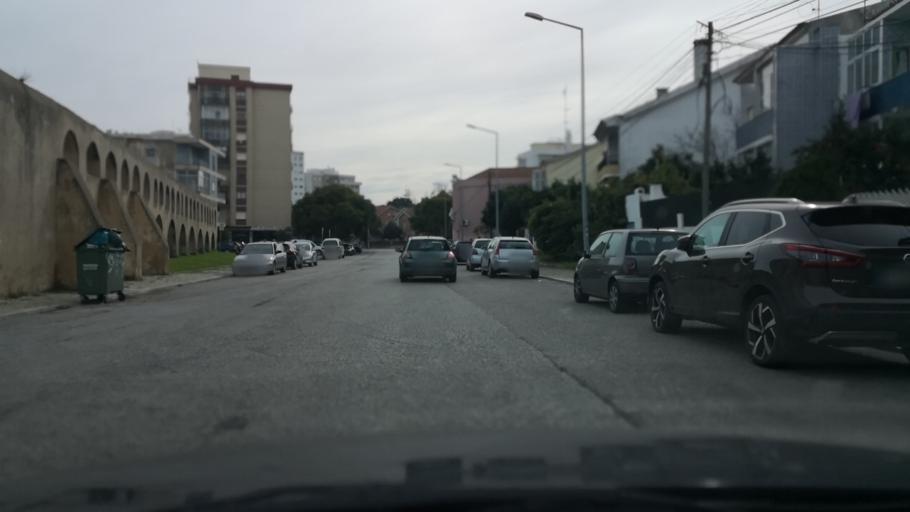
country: PT
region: Setubal
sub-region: Setubal
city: Setubal
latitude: 38.5294
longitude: -8.8953
